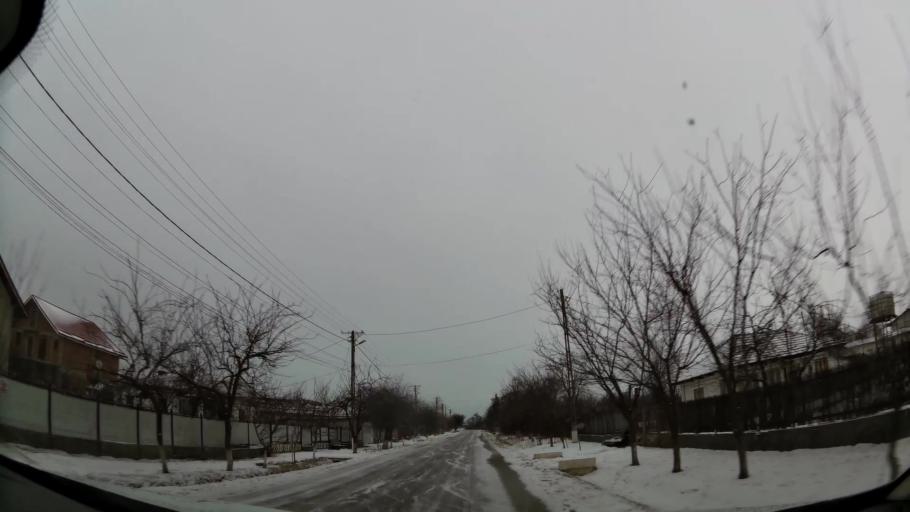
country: RO
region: Prahova
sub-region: Comuna Poenarii-Burchi
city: Ologeni
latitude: 44.7334
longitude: 25.9292
